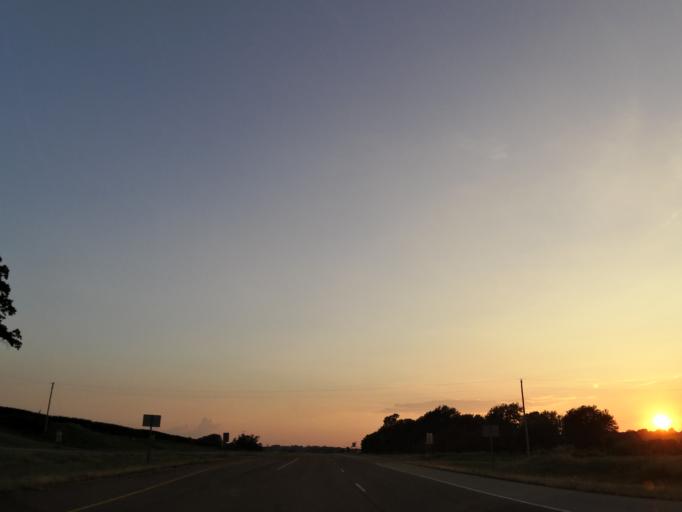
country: US
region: Tennessee
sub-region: Henry County
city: Paris
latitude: 36.2266
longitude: -88.3747
